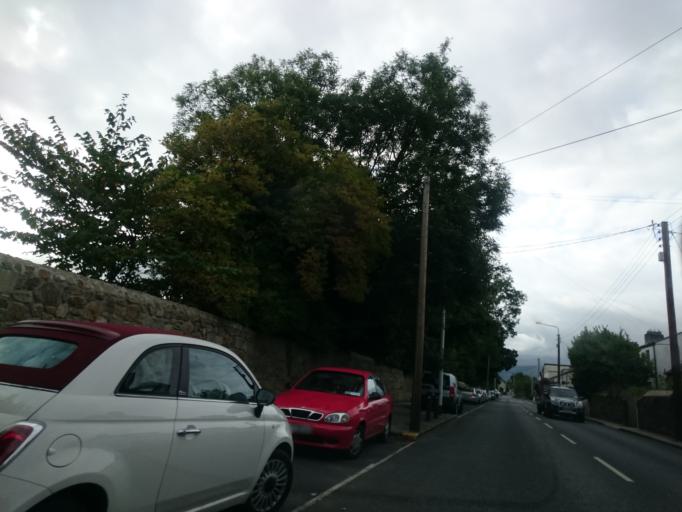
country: IE
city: Milltown
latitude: 53.3071
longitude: -6.2463
